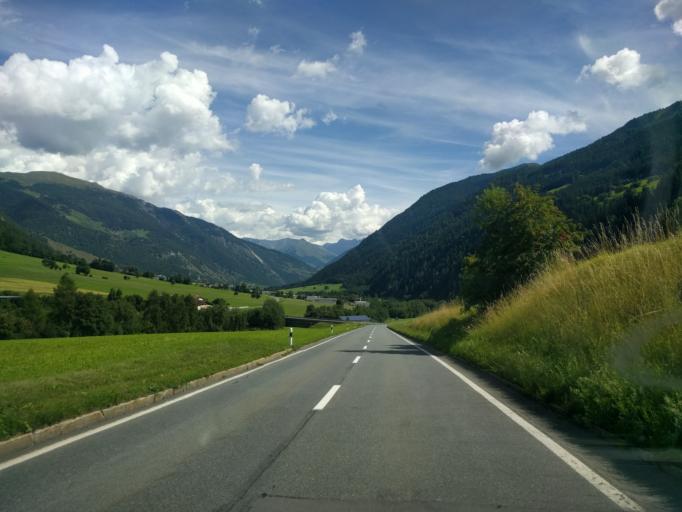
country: IT
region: Trentino-Alto Adige
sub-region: Bolzano
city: Tubre
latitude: 46.6112
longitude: 10.4372
